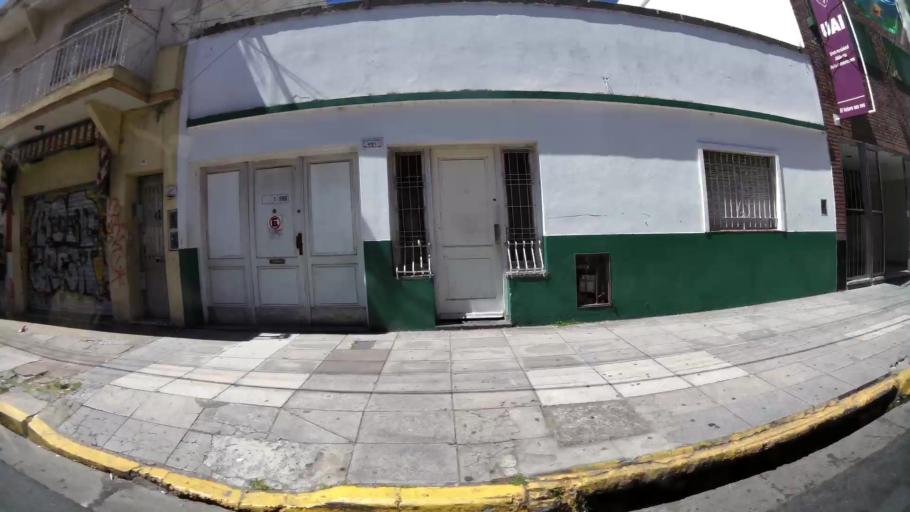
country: AR
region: Buenos Aires
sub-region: Partido de San Isidro
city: San Isidro
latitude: -34.5034
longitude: -58.5739
